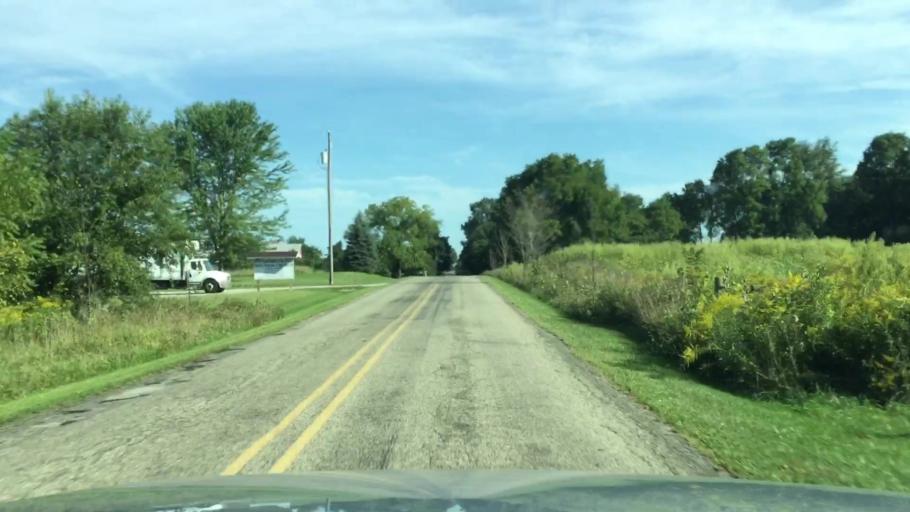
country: US
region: Michigan
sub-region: Lenawee County
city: Hudson
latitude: 41.8896
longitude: -84.4203
